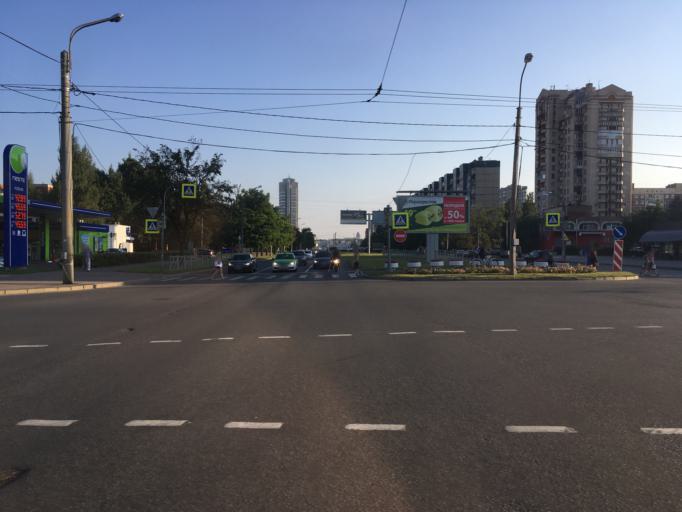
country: RU
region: St.-Petersburg
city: Komendantsky aerodrom
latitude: 60.0119
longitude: 30.2762
